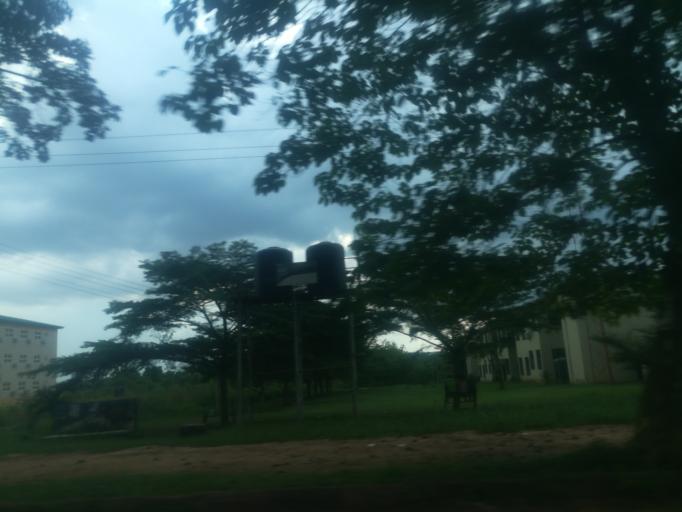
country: NG
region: Oyo
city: Ibadan
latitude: 7.4358
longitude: 3.8863
